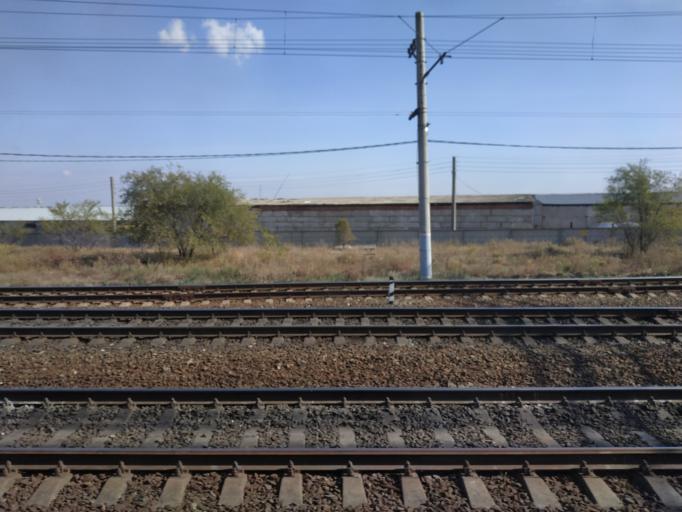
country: RU
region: Volgograd
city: Gumrak
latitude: 48.7876
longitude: 44.3703
